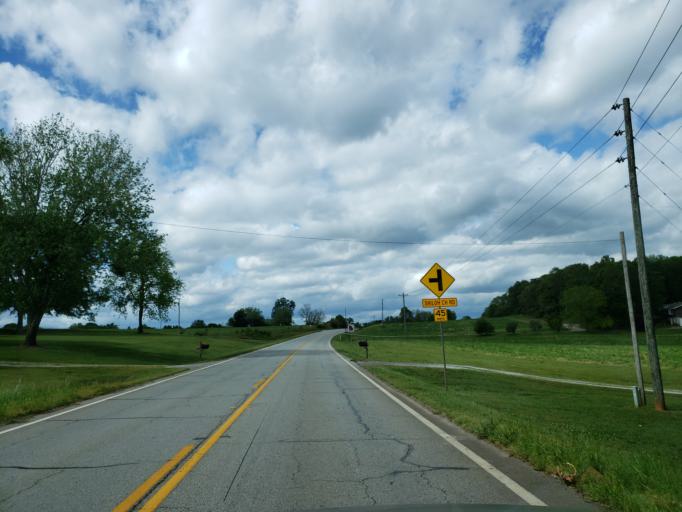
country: US
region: Georgia
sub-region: Haralson County
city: Tallapoosa
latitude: 33.6636
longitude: -85.2673
